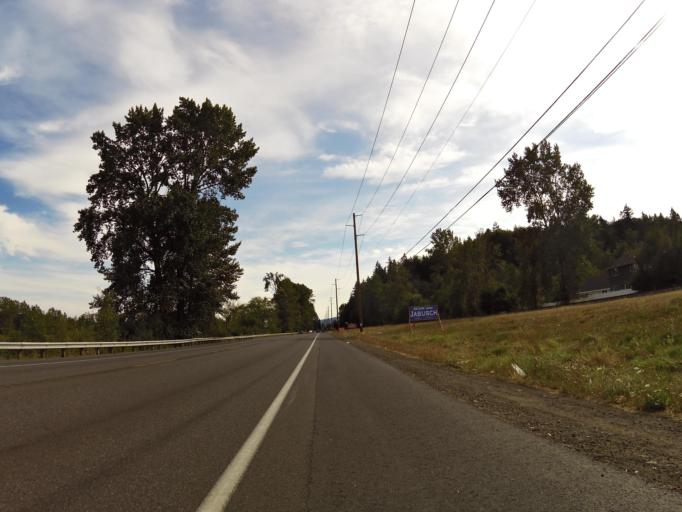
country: US
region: Washington
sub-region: Cowlitz County
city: Kelso
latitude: 46.1616
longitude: -122.9160
